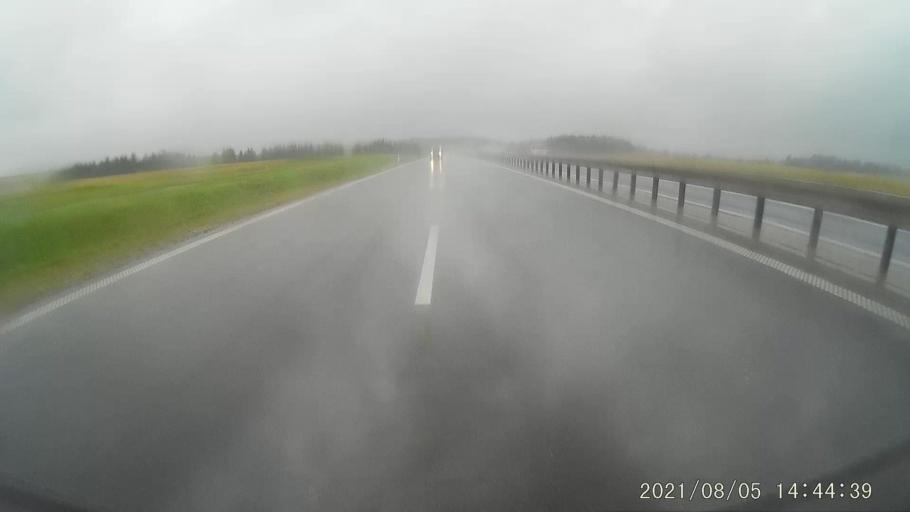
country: PL
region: Opole Voivodeship
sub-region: Powiat nyski
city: Nysa
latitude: 50.4954
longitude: 17.3744
